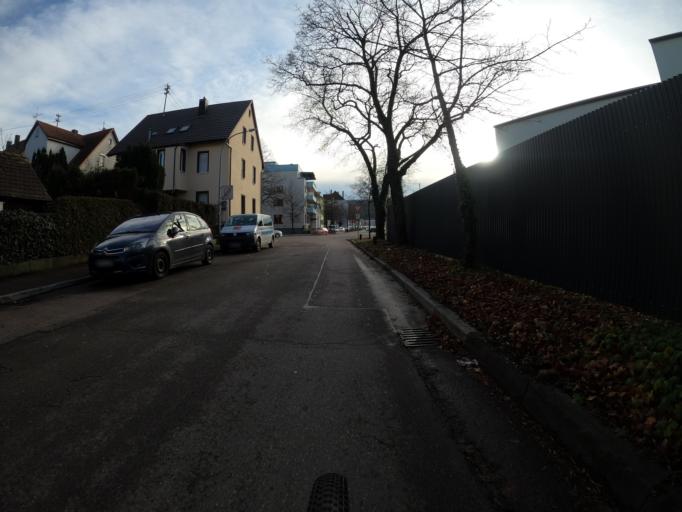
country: DE
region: Baden-Wuerttemberg
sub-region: Regierungsbezirk Stuttgart
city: Goeppingen
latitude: 48.6984
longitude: 9.6627
